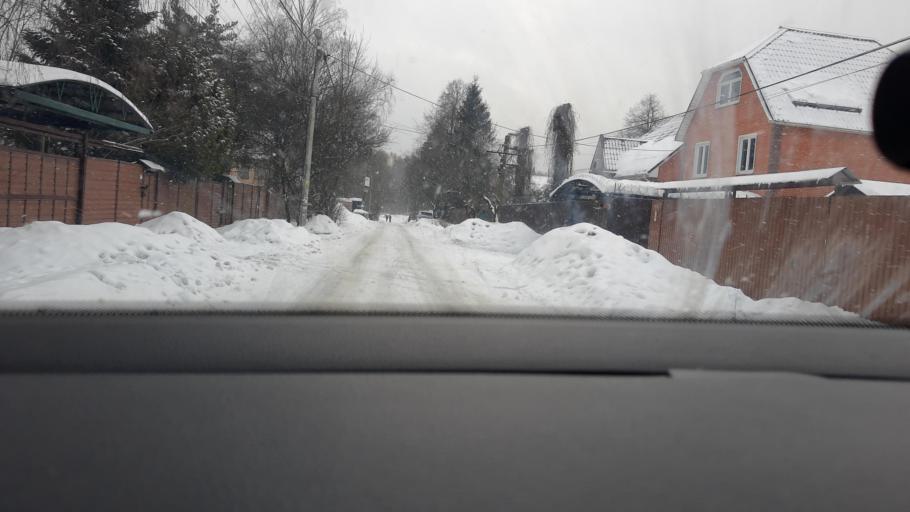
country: RU
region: Moskovskaya
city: Druzhba
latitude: 55.8833
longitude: 37.7406
